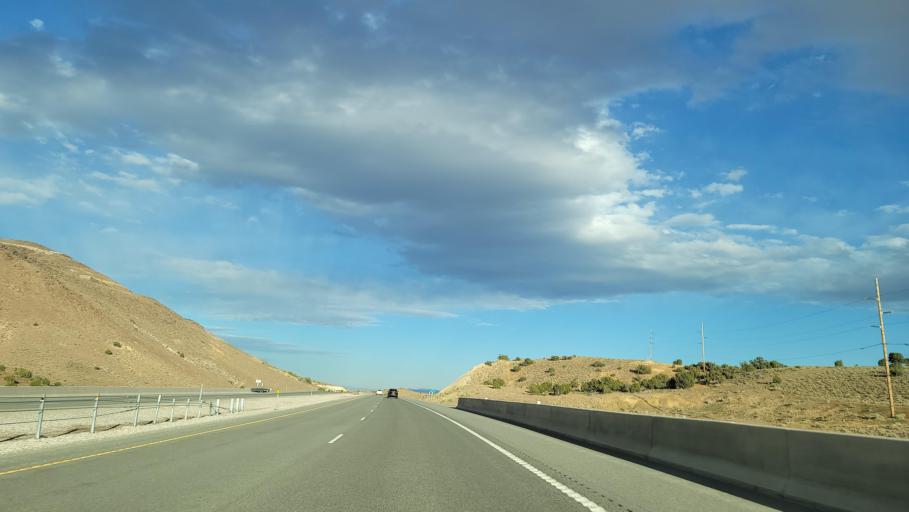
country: US
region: Nevada
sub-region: Lyon County
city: Stagecoach
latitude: 39.4695
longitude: -119.3906
